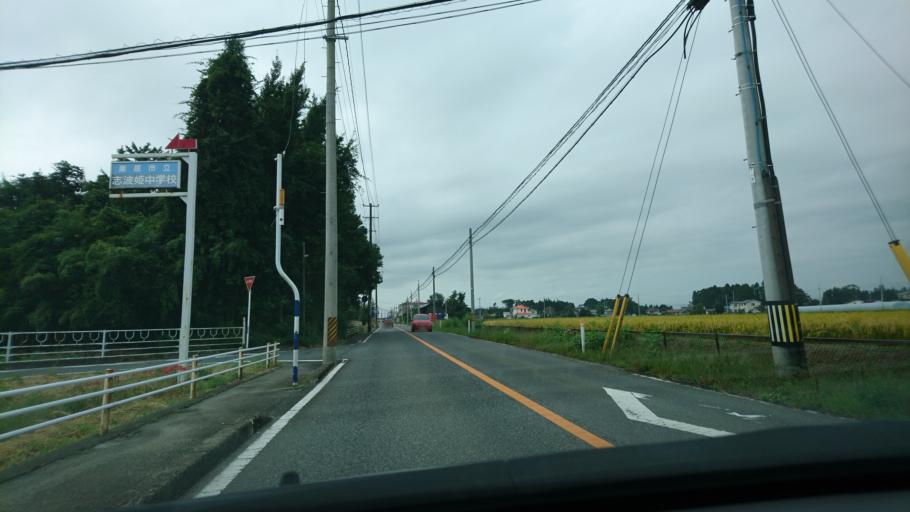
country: JP
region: Iwate
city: Ichinoseki
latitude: 38.7519
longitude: 141.0579
